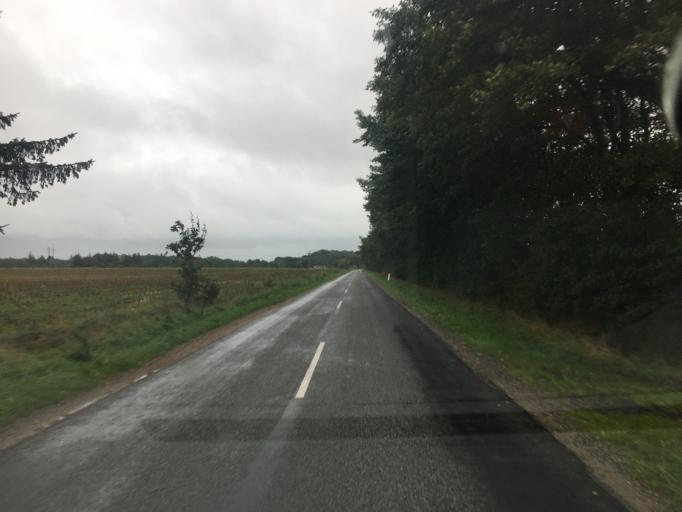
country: DE
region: Schleswig-Holstein
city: Bramstedtlund
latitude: 54.9635
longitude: 9.0498
